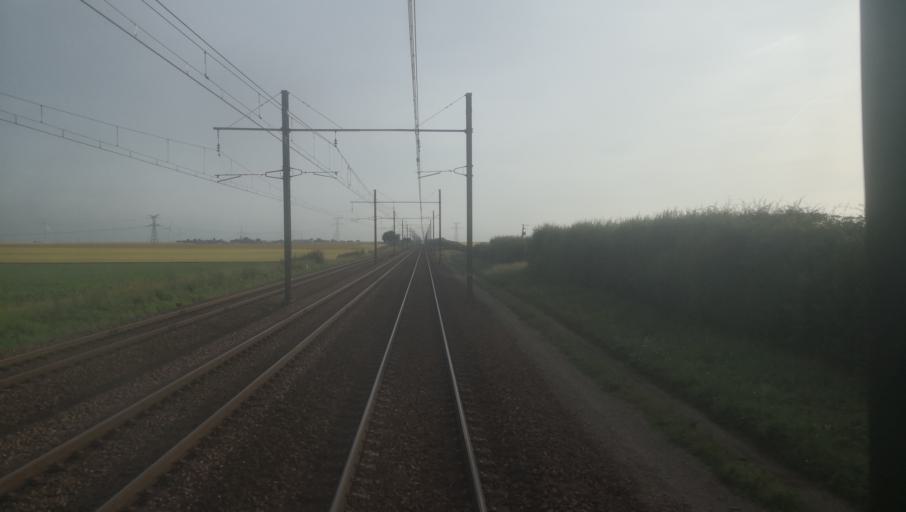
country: FR
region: Centre
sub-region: Departement du Loiret
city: Artenay
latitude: 48.1205
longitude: 1.9017
